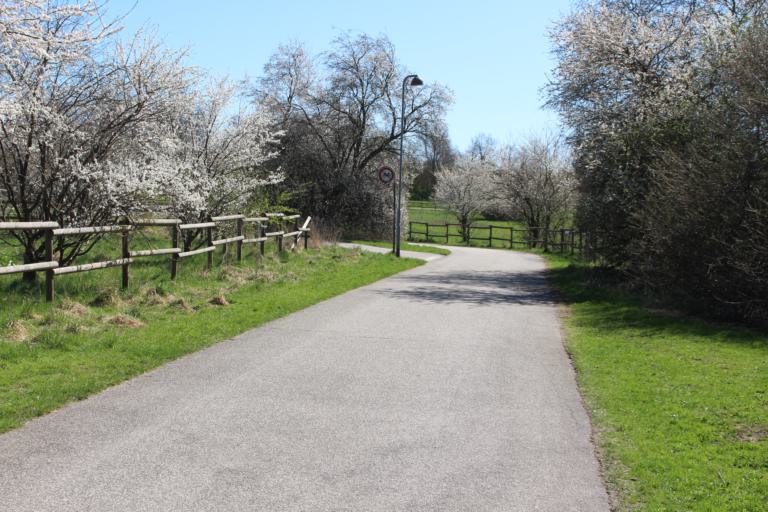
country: DK
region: Capital Region
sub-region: Albertslund Kommune
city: Albertslund
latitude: 55.6777
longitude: 12.3405
